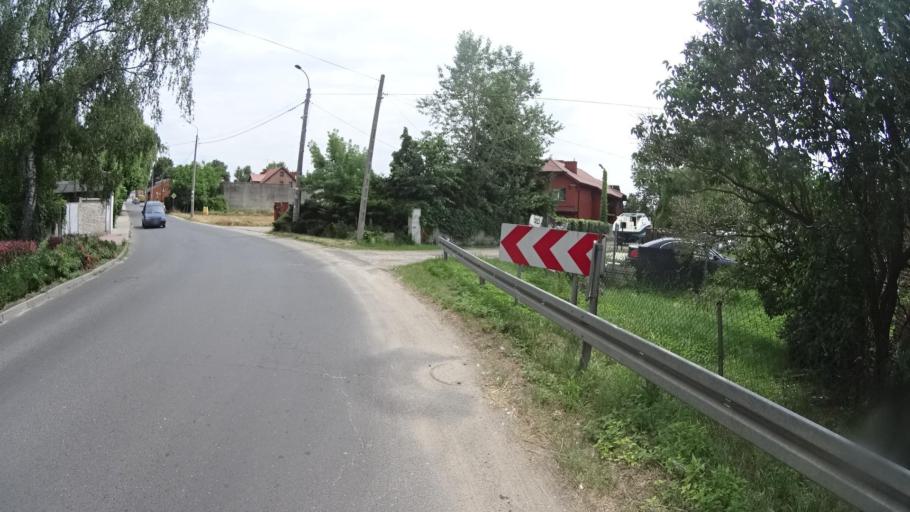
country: PL
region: Masovian Voivodeship
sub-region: Powiat piaseczynski
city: Tarczyn
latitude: 51.9810
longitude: 20.8317
